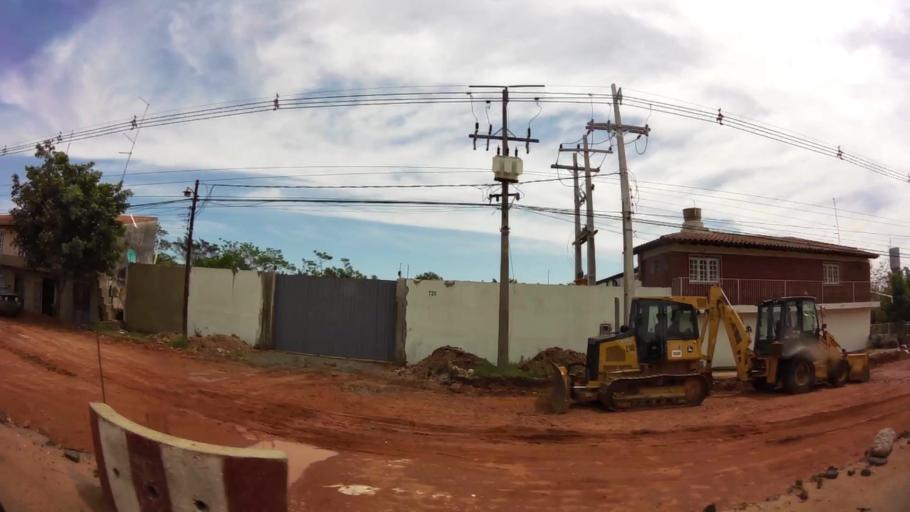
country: PY
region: Central
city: Limpio
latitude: -25.1958
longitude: -57.5120
